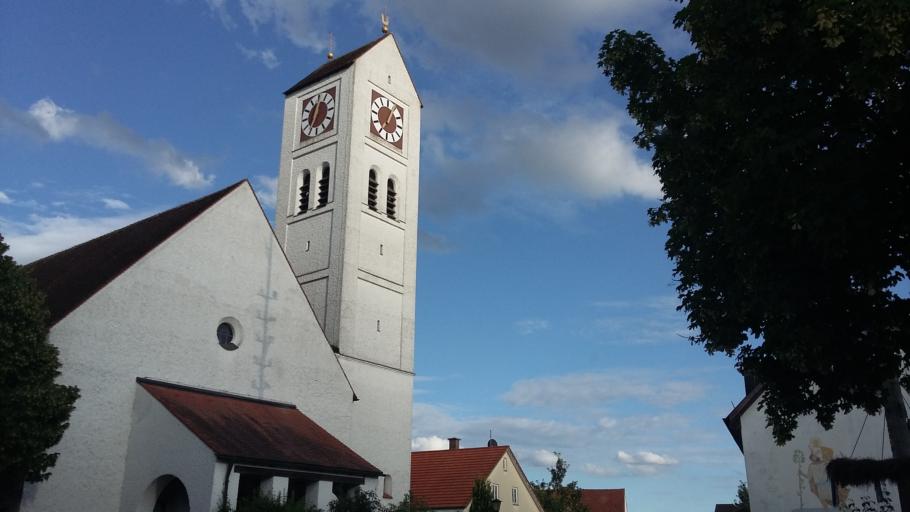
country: DE
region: Bavaria
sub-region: Upper Bavaria
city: Althegnenberg
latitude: 48.2344
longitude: 11.0633
